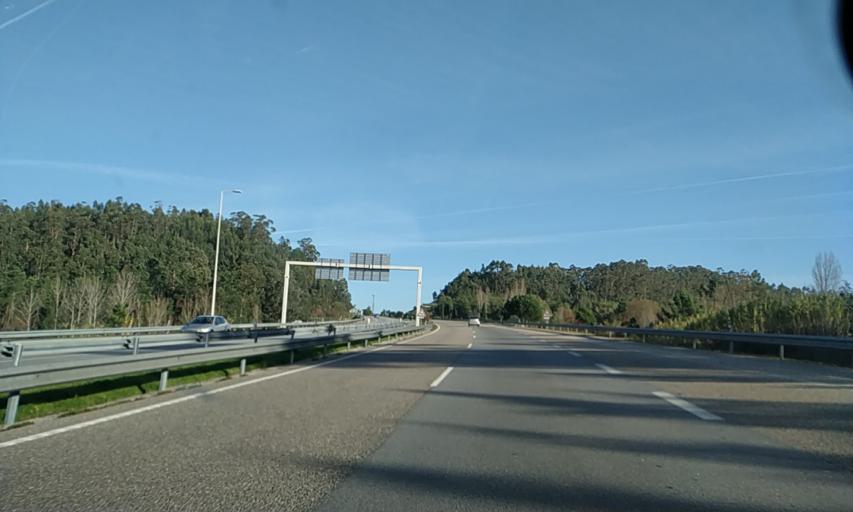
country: PT
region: Aveiro
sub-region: Mealhada
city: Pampilhosa do Botao
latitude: 40.2696
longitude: -8.4663
